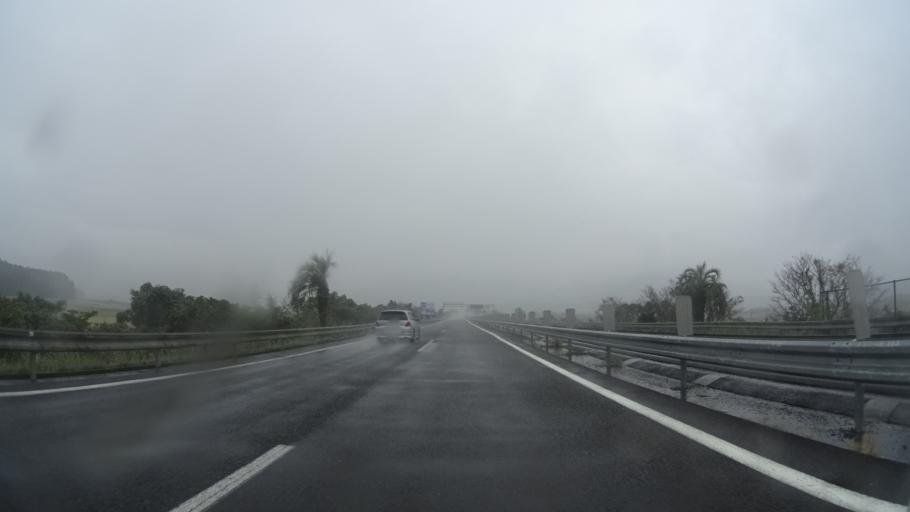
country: JP
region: Kagoshima
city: Okuchi-shinohara
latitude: 32.0399
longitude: 130.7995
